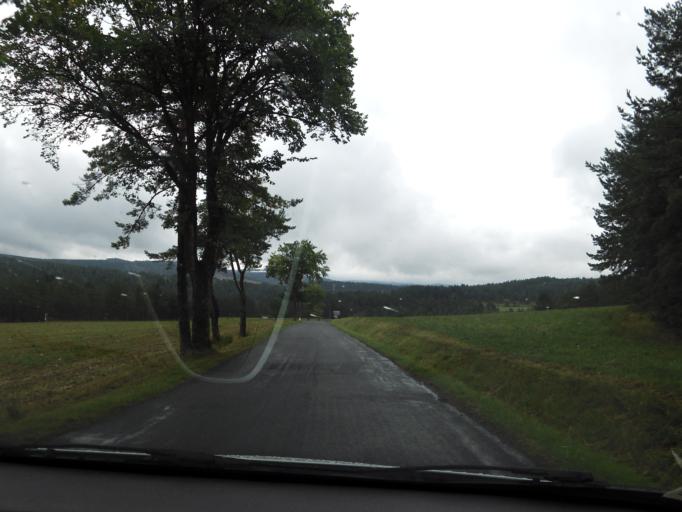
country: FR
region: Languedoc-Roussillon
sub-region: Departement de la Lozere
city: Mende
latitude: 44.4579
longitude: 3.4611
